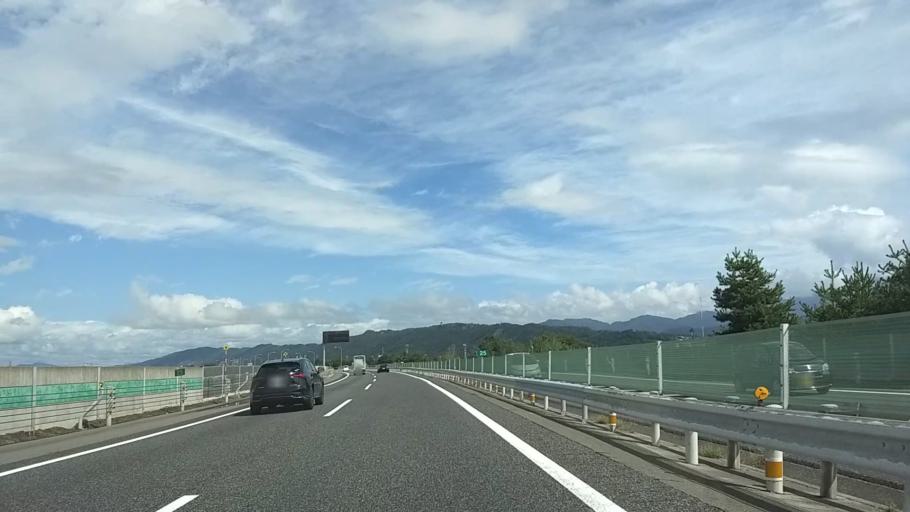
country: JP
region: Nagano
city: Matsumoto
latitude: 36.2268
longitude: 137.9378
